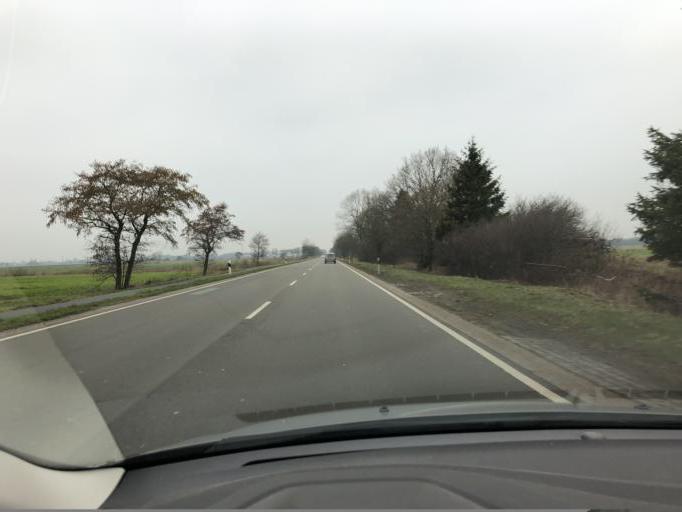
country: DE
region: Lower Saxony
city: Upgant-Schott
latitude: 53.4987
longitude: 7.3010
